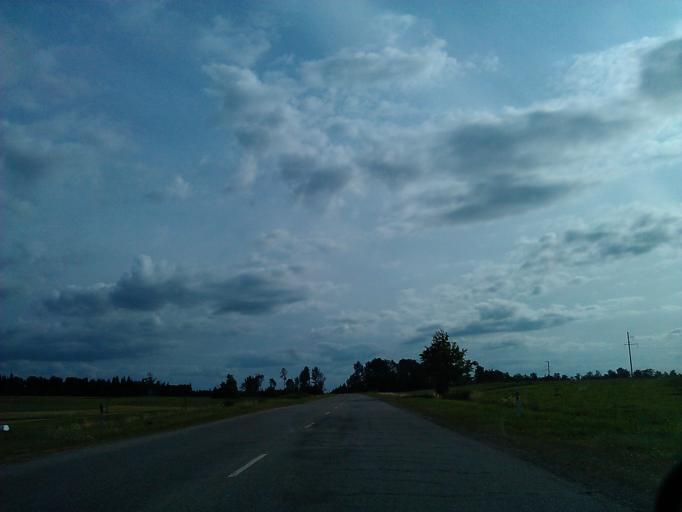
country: LV
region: Amatas Novads
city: Drabesi
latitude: 57.2757
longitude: 25.2826
